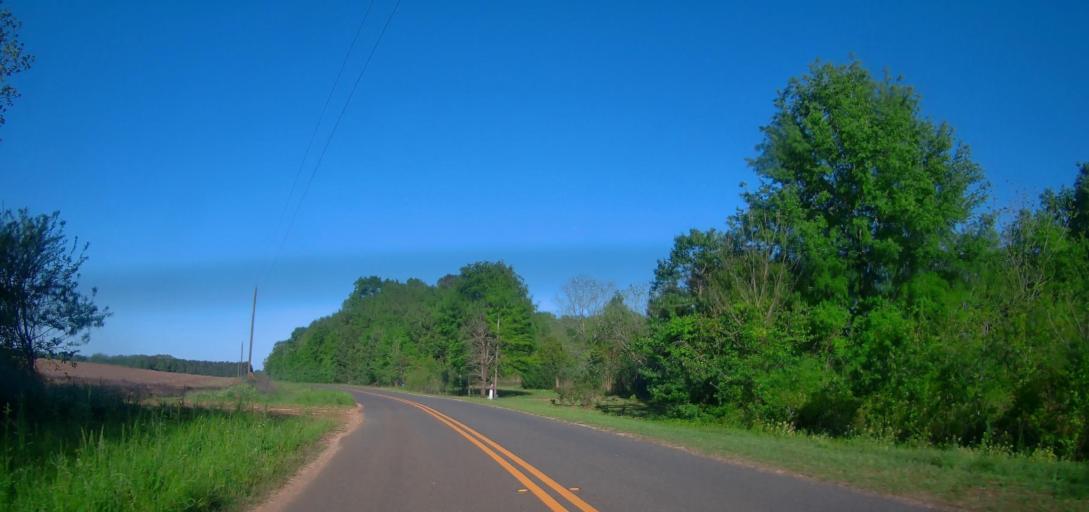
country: US
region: Georgia
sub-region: Macon County
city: Marshallville
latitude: 32.3825
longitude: -83.8660
